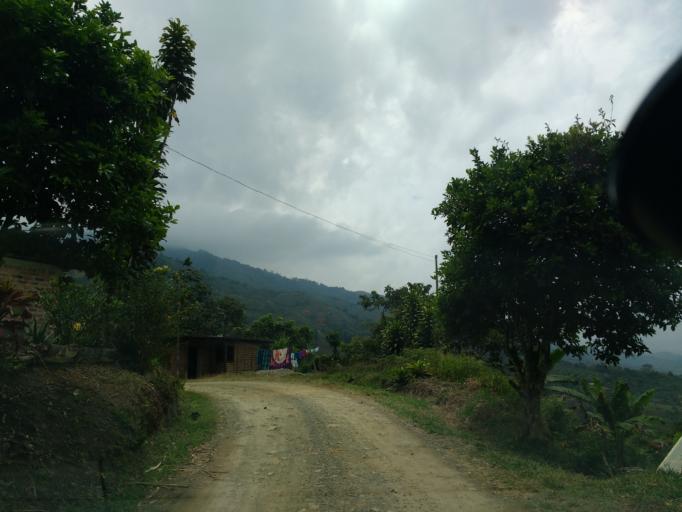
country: CO
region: Cauca
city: Santander de Quilichao
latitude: 2.9187
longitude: -76.4715
